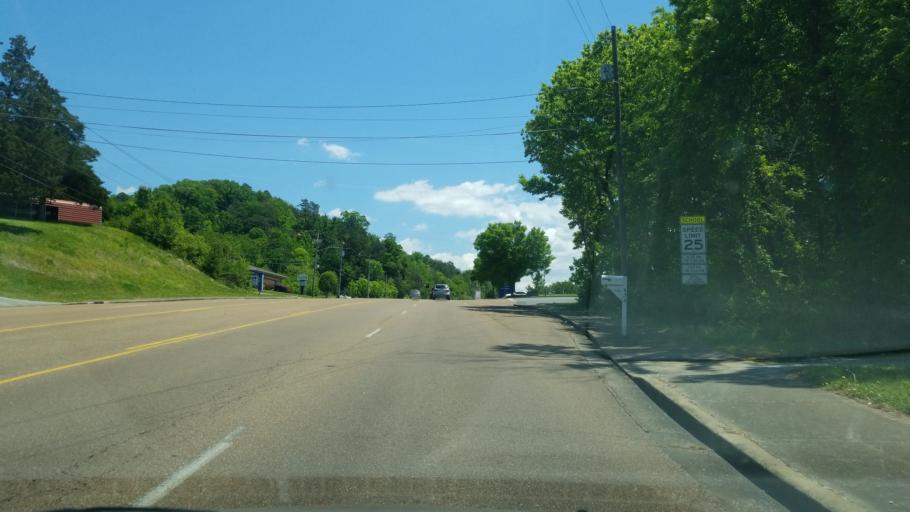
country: US
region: Tennessee
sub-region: Hamilton County
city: Red Bank
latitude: 35.1247
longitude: -85.3030
